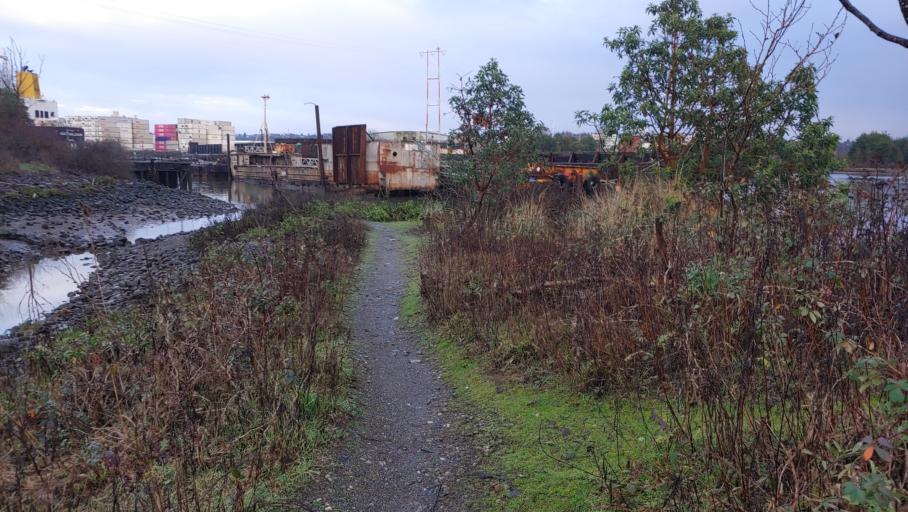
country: US
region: Washington
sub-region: King County
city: White Center
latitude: 47.5619
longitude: -122.3502
